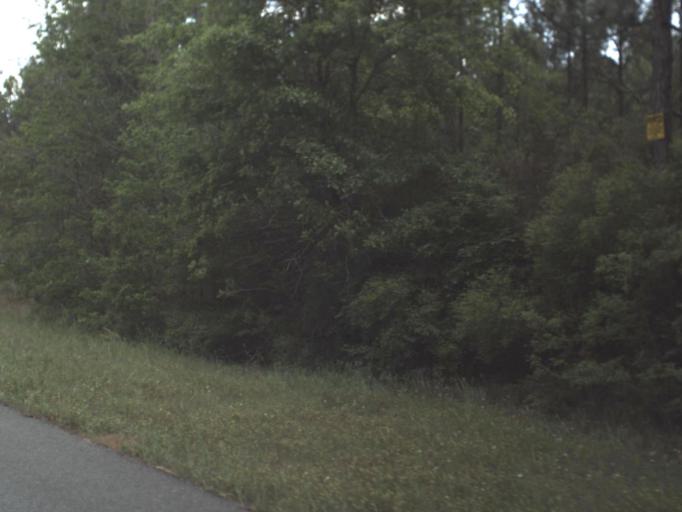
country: US
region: Florida
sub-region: Escambia County
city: Molino
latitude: 30.8189
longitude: -87.4332
